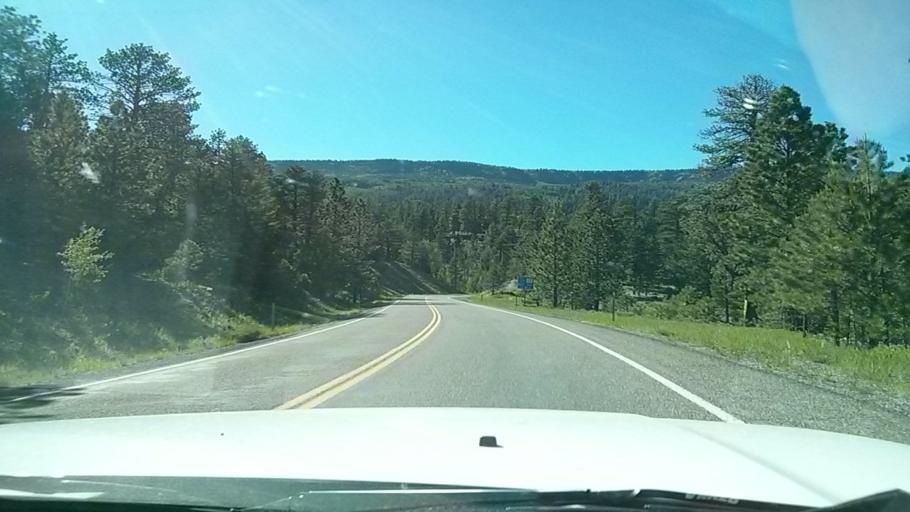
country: US
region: Utah
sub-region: Wayne County
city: Loa
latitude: 38.1043
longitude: -111.3369
